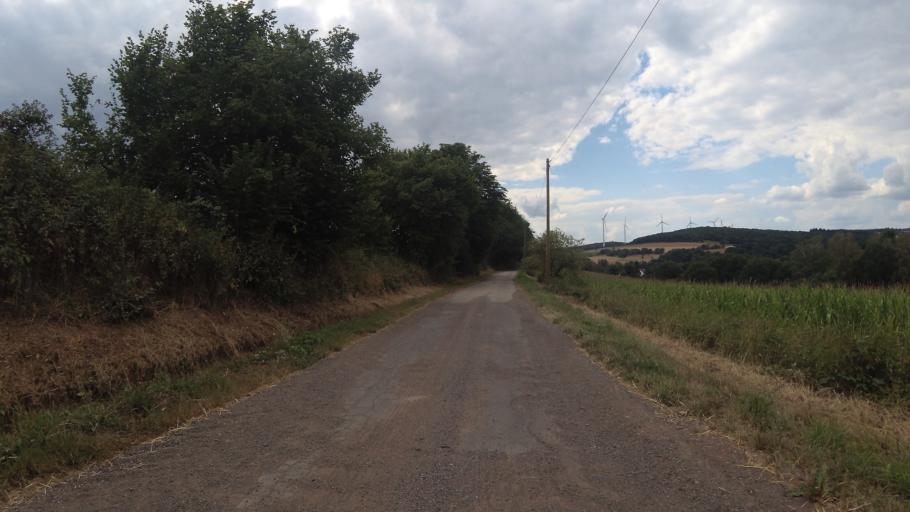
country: DE
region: Rheinland-Pfalz
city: Breitenbach
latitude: 49.4342
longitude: 7.2444
